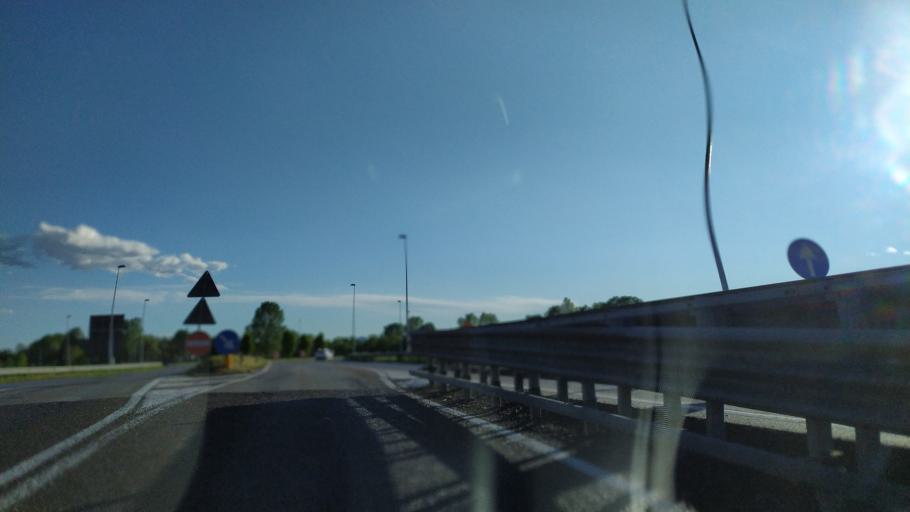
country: IT
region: Veneto
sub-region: Provincia di Padova
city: Limena
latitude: 45.4586
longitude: 11.8374
